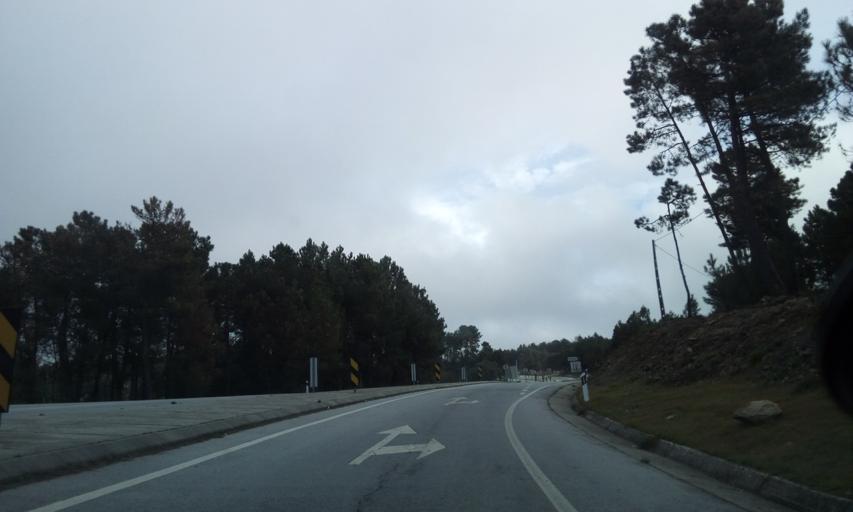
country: PT
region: Guarda
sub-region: Aguiar da Beira
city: Aguiar da Beira
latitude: 40.7306
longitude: -7.4955
